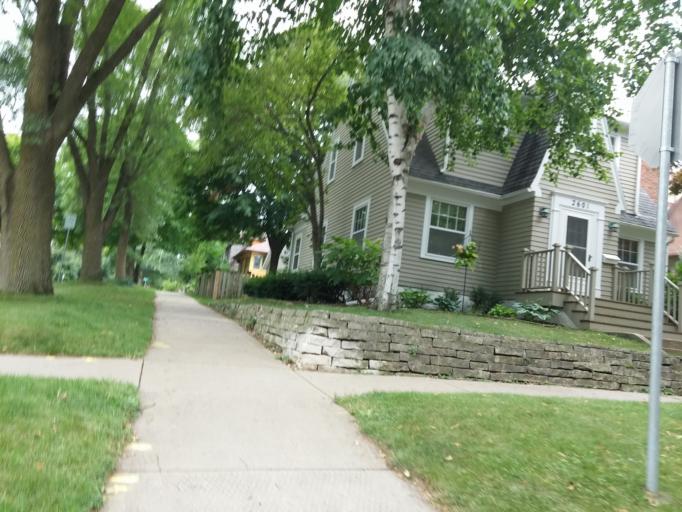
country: US
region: Wisconsin
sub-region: Dane County
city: Shorewood Hills
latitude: 43.0698
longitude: -89.4315
